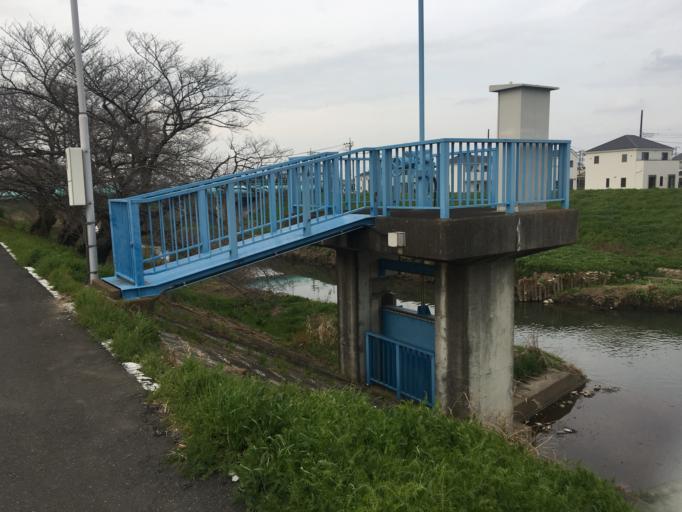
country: JP
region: Saitama
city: Oi
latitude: 35.8667
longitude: 139.5502
